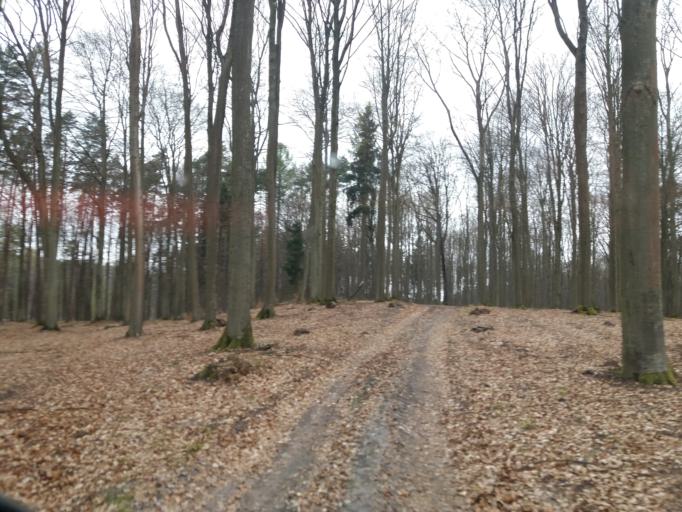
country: PL
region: West Pomeranian Voivodeship
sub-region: Powiat choszczenski
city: Drawno
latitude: 53.1067
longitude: 15.8408
